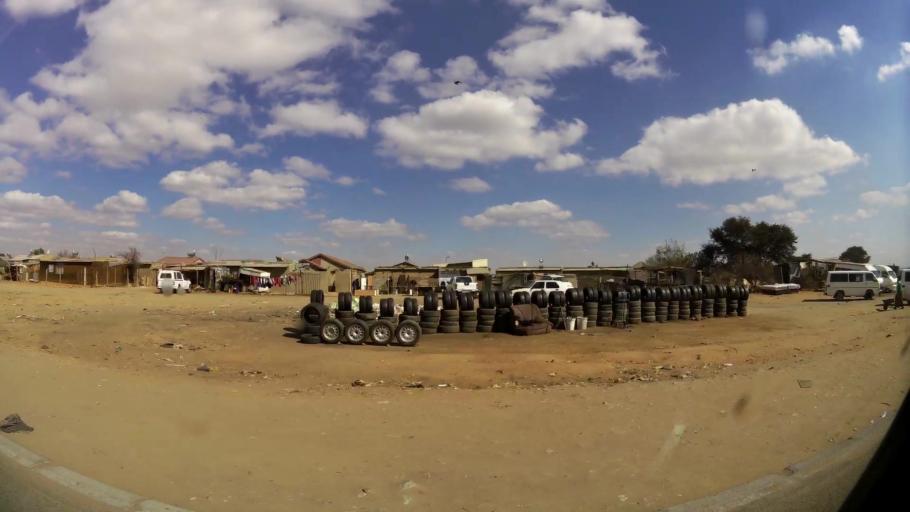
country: ZA
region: Gauteng
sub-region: City of Johannesburg Metropolitan Municipality
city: Midrand
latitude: -26.0287
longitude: 28.1715
